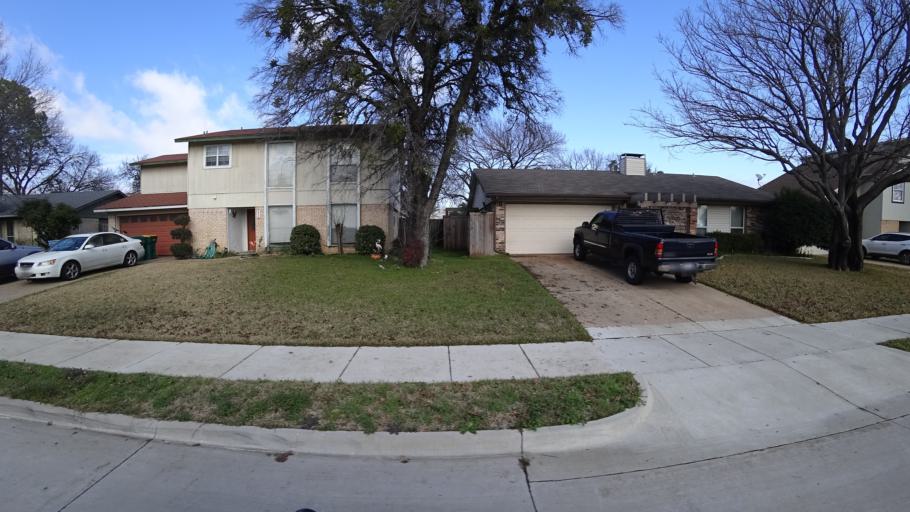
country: US
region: Texas
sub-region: Denton County
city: Lewisville
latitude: 33.0333
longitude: -97.0053
